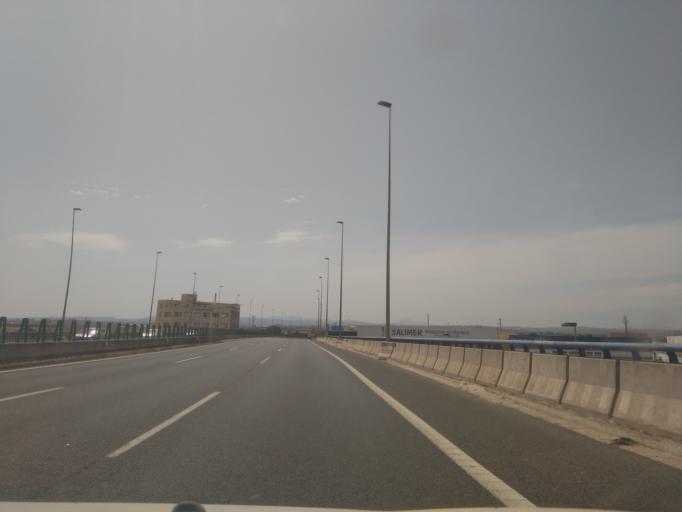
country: ES
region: Valencia
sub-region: Provincia de Valencia
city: Beniparrell
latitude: 39.3760
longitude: -0.4137
